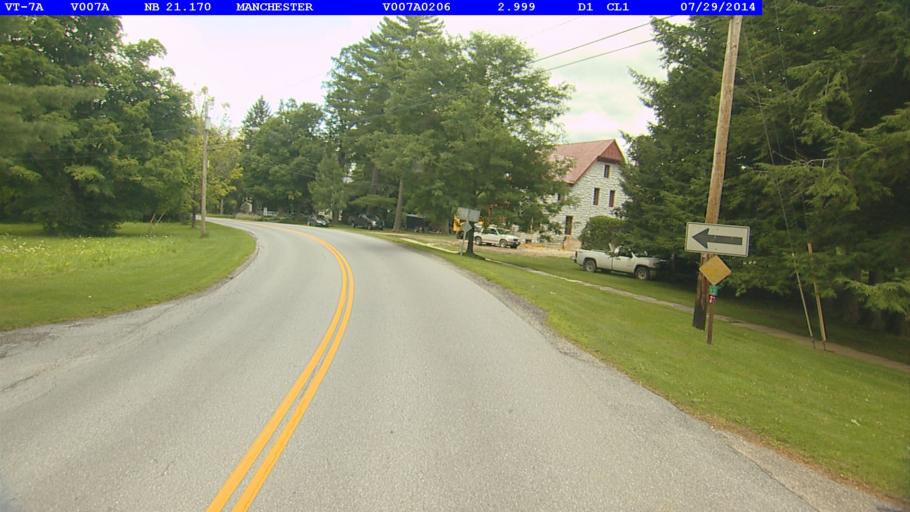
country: US
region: Vermont
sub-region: Bennington County
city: Manchester Center
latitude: 43.1544
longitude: -73.0747
